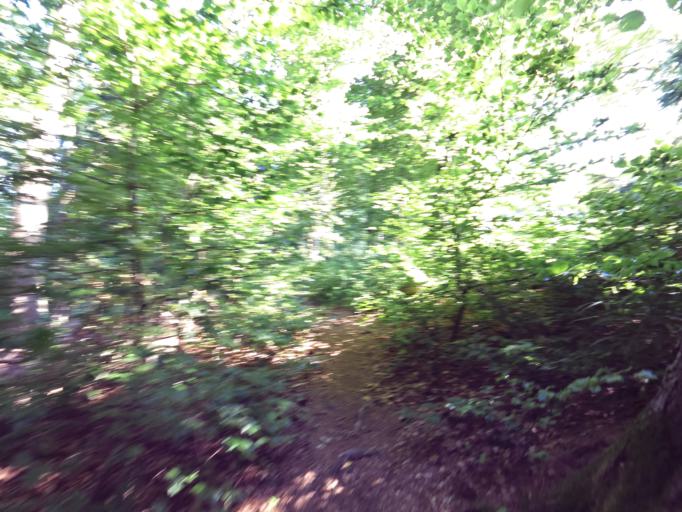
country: CH
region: Zurich
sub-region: Bezirk Zuerich
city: Zuerich (Kreis 2) / Unter-Leimbach
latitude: 47.3415
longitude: 8.5005
